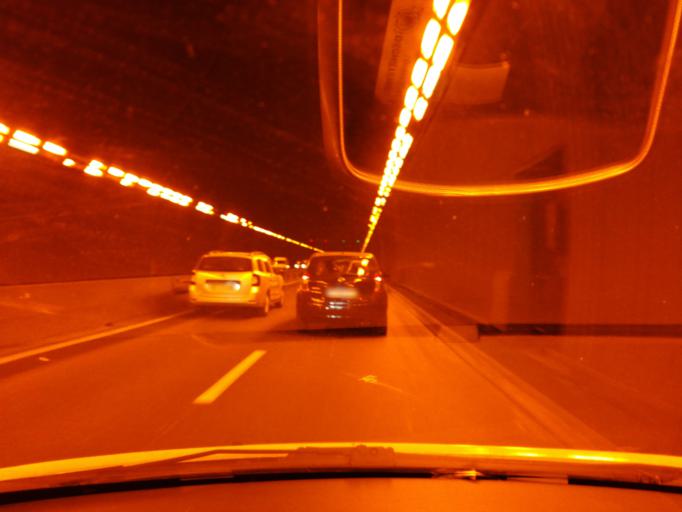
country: FR
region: Provence-Alpes-Cote d'Azur
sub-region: Departement des Alpes-Maritimes
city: Nice
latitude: 43.7082
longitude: 7.2720
